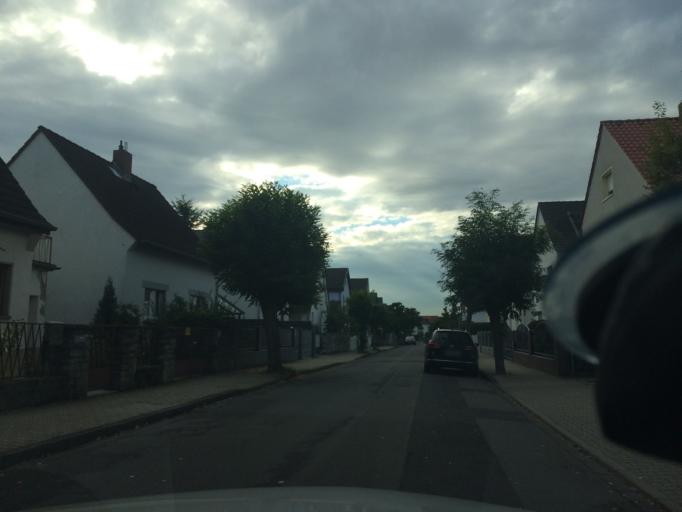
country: DE
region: Hesse
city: Morfelden-Walldorf
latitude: 50.0083
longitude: 8.5817
